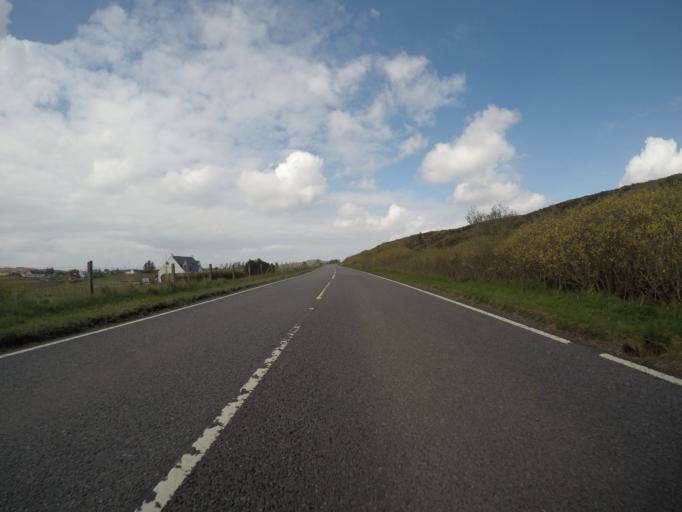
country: GB
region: Scotland
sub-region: Highland
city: Portree
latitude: 57.5605
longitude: -6.3635
